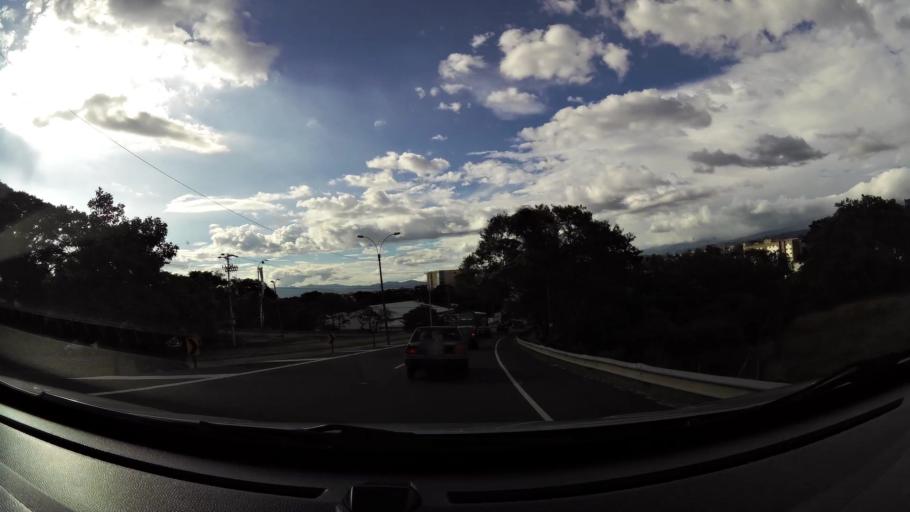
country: CR
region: Alajuela
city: Alajuela
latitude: 10.0002
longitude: -84.2056
